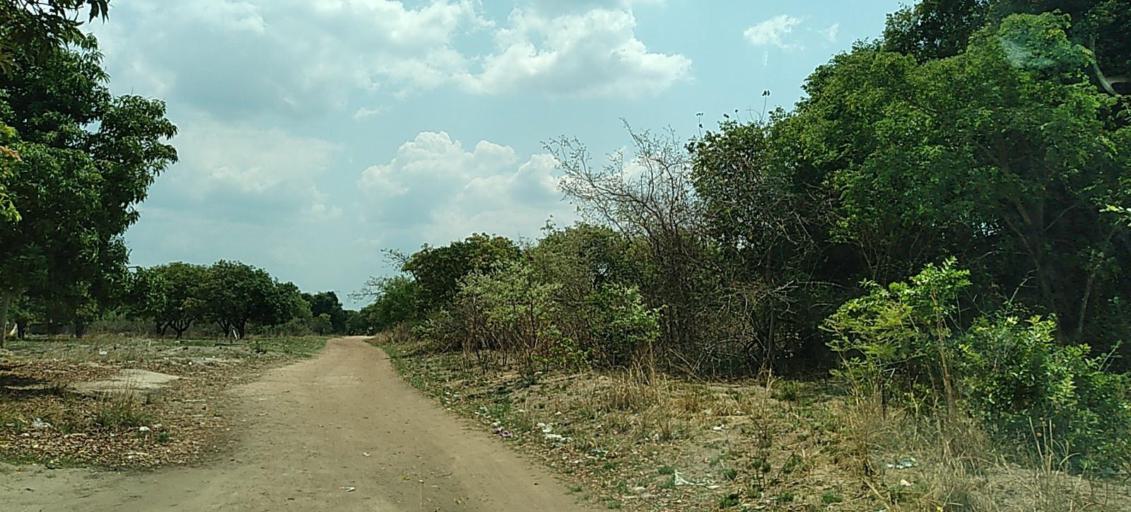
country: ZM
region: Copperbelt
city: Luanshya
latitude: -13.1569
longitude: 28.3118
